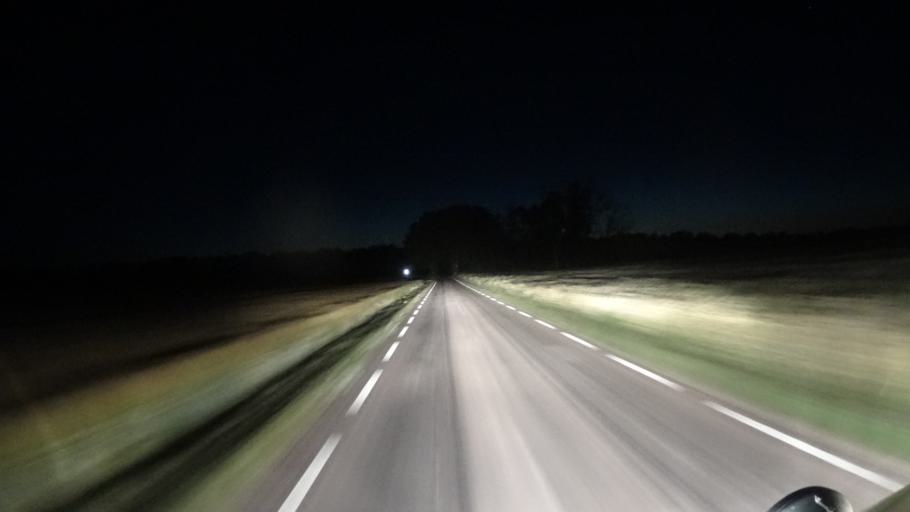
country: SE
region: OEstergoetland
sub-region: Vadstena Kommun
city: Herrestad
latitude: 58.3153
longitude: 14.8430
